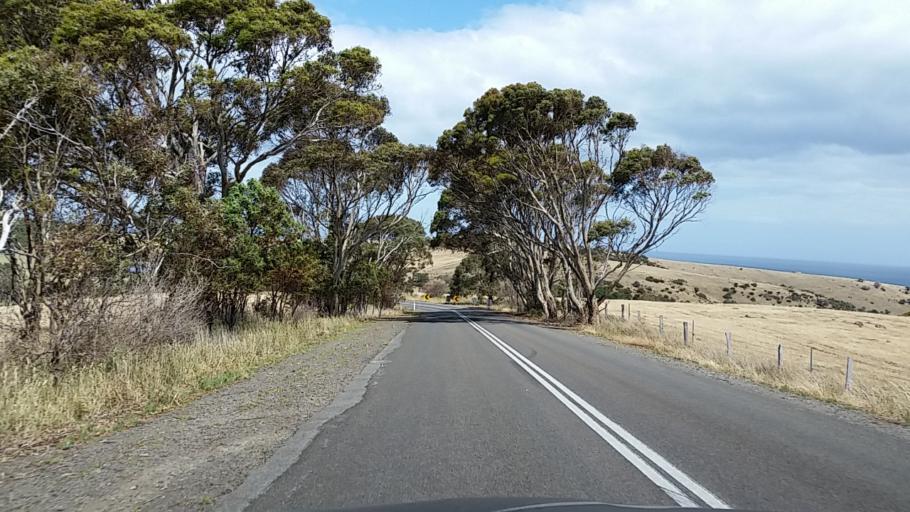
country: AU
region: South Australia
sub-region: Alexandrina
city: Port Elliot
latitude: -35.5021
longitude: 138.6675
